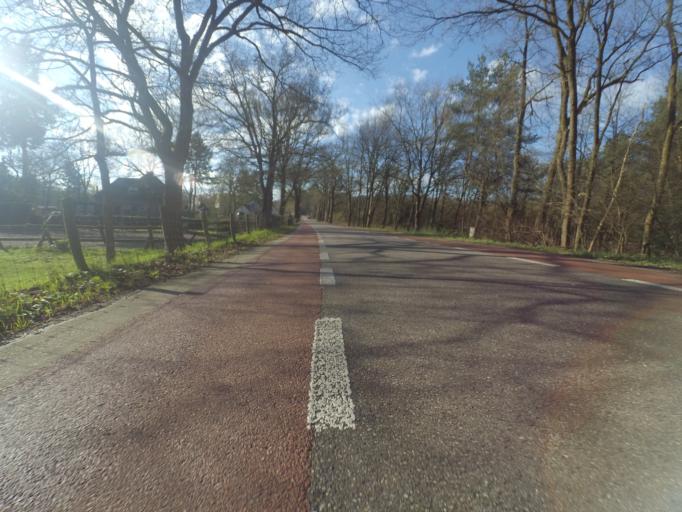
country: NL
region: Gelderland
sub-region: Gemeente Apeldoorn
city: Beekbergen
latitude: 52.1120
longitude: 5.8754
